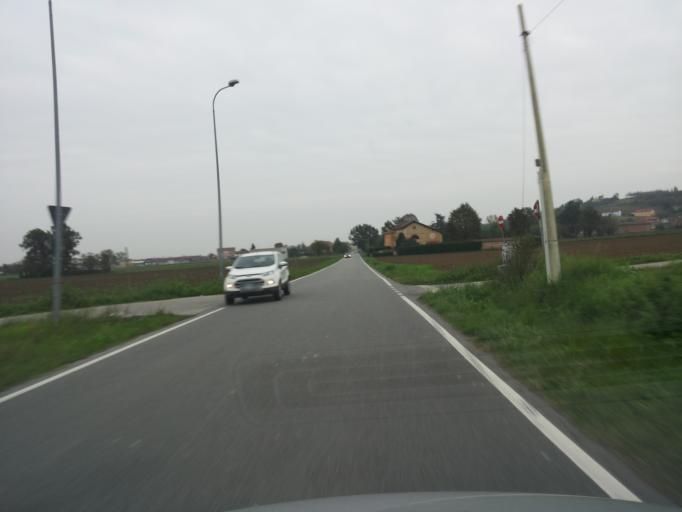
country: IT
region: Piedmont
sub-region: Provincia di Alessandria
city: Terruggia
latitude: 45.1039
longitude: 8.4430
